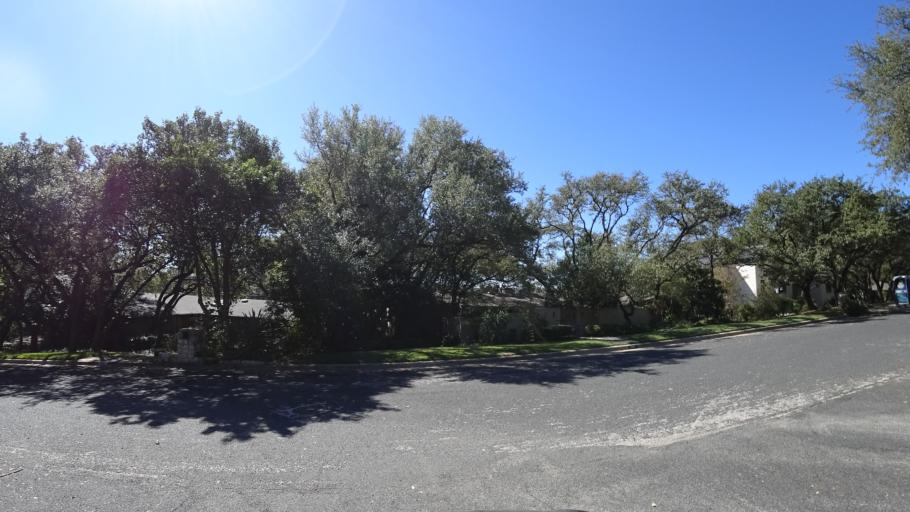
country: US
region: Texas
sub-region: Travis County
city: West Lake Hills
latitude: 30.3435
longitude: -97.7821
